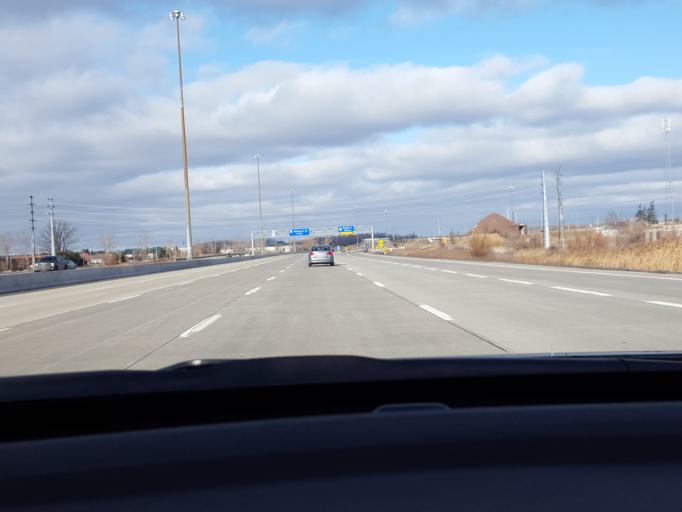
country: CA
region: Ontario
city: Concord
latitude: 43.8086
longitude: -79.4798
